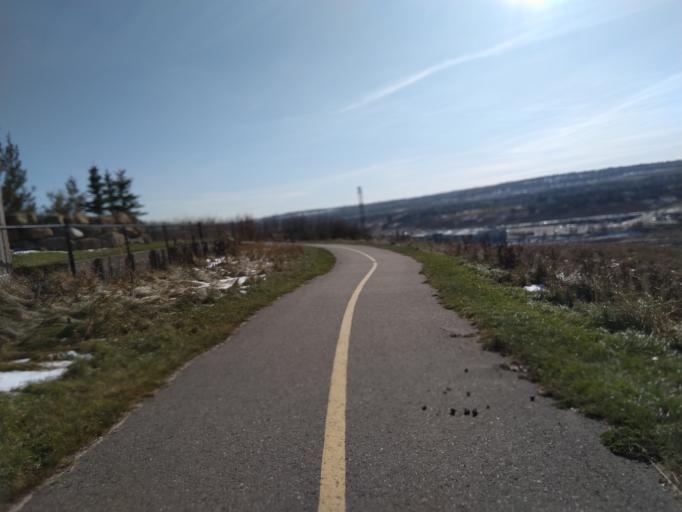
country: CA
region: Alberta
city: Calgary
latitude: 51.1707
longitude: -114.1239
